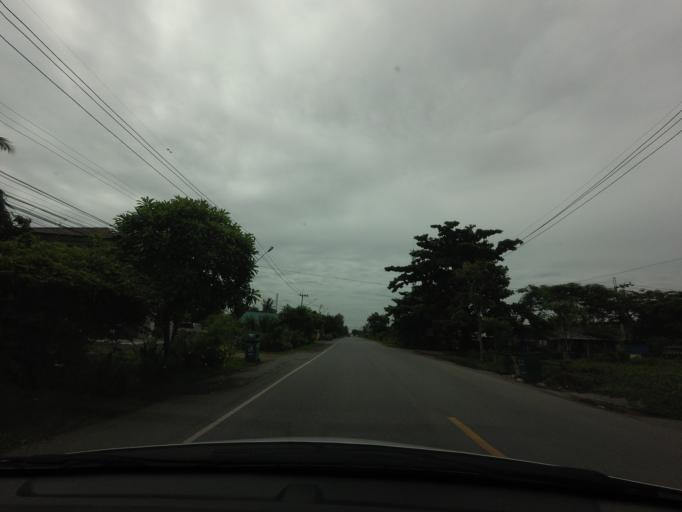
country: TH
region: Bangkok
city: Nong Chok
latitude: 13.8780
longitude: 100.8090
